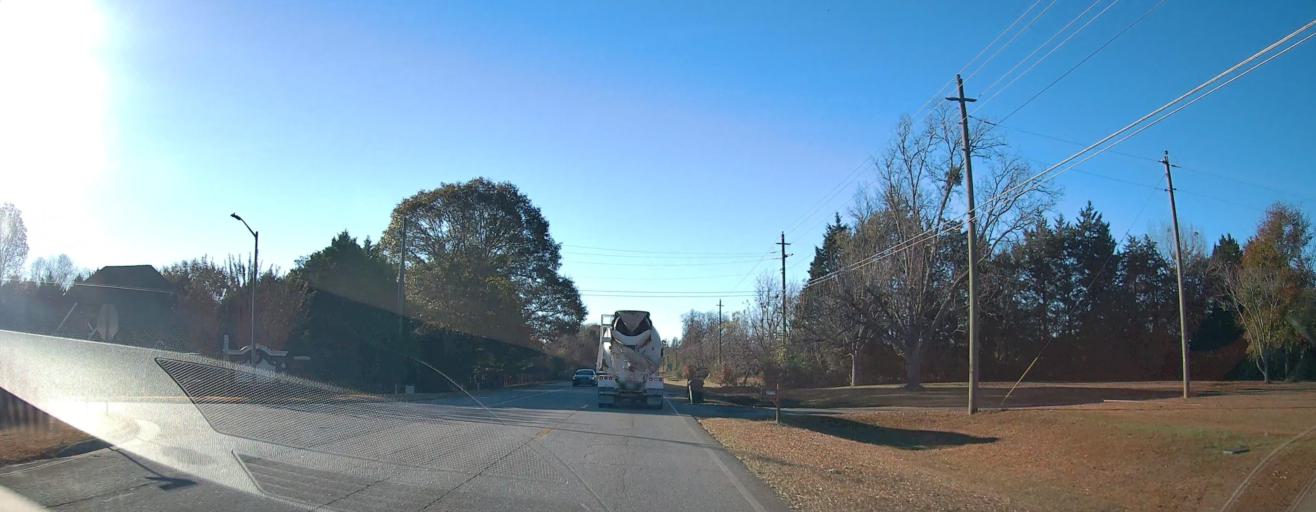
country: US
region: Georgia
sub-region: Houston County
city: Centerville
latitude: 32.5540
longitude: -83.7197
